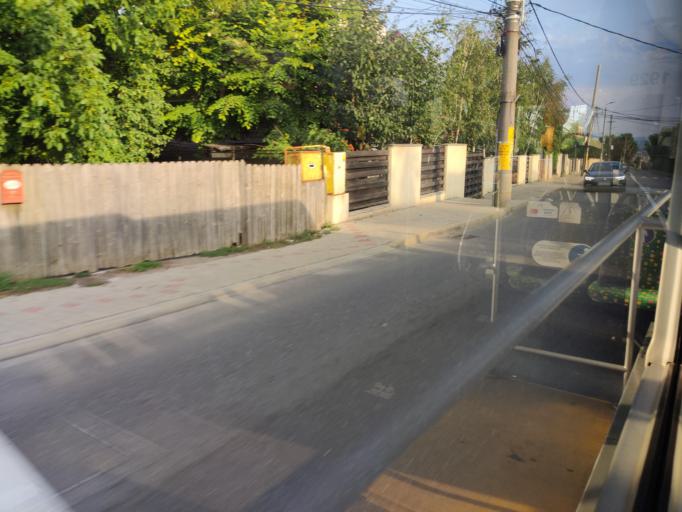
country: RO
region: Iasi
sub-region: Municipiul Iasi
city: Iasi
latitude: 47.1751
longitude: 27.5982
